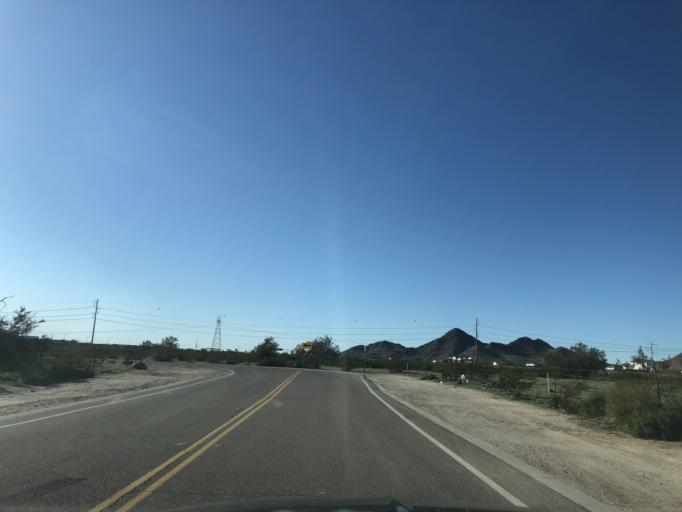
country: US
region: Arizona
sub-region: Maricopa County
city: Buckeye
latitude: 33.4301
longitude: -112.5945
